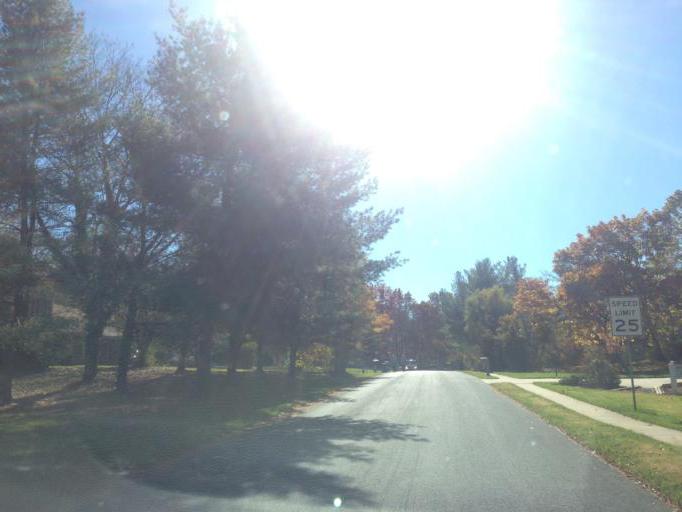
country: US
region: Maryland
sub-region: Howard County
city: Riverside
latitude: 39.2004
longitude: -76.8775
